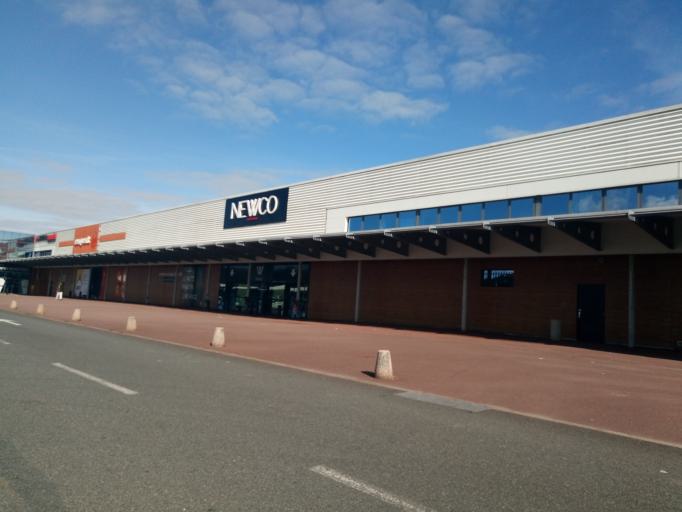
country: FR
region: Brittany
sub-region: Departement des Cotes-d'Armor
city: Rostrenen
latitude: 48.2425
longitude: -3.3138
